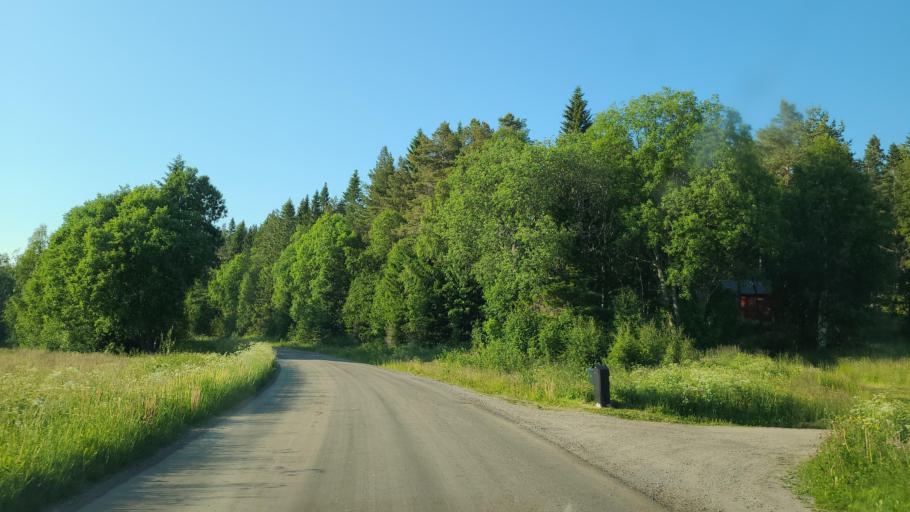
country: SE
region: Vaesterbotten
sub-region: Skelleftea Kommun
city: Burea
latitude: 64.3472
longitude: 21.3552
